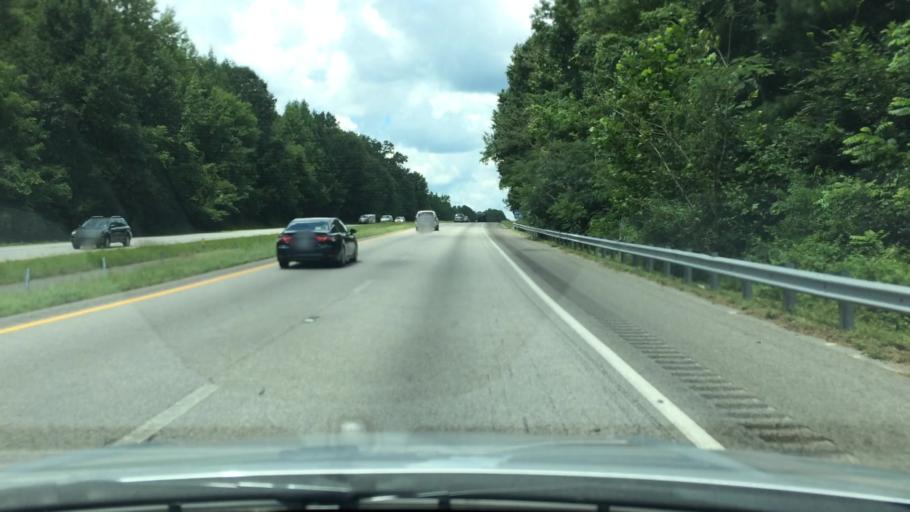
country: US
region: South Carolina
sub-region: Laurens County
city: Clinton
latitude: 34.4872
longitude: -81.8327
